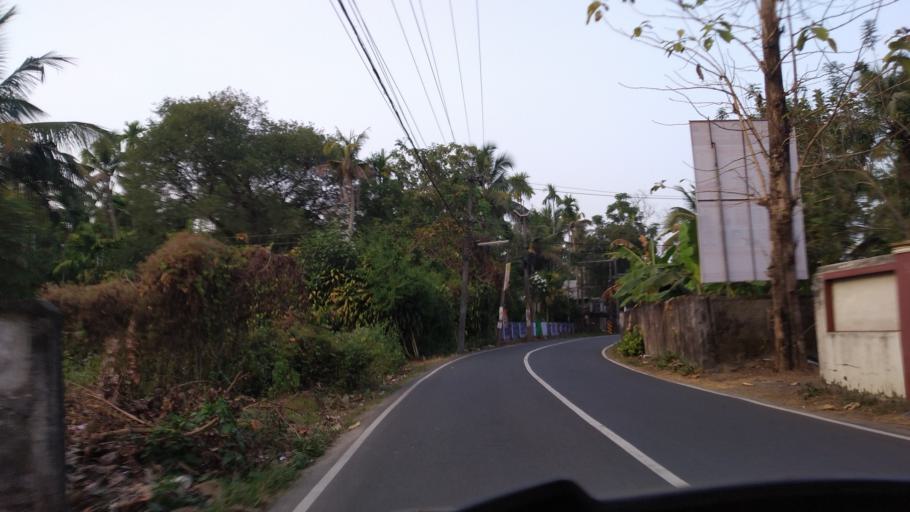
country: IN
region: Kerala
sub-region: Ernakulam
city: Elur
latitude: 10.1206
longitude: 76.2398
